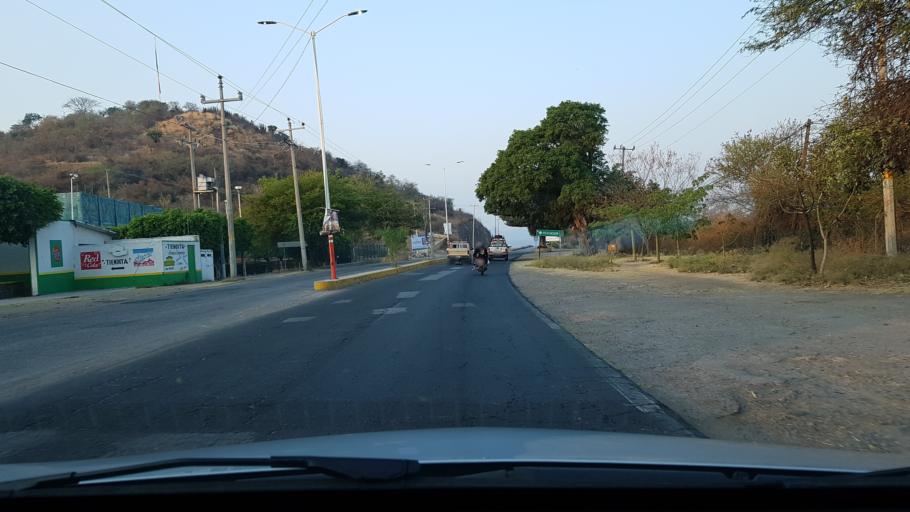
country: MX
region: Morelos
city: Jonacatepec de Leandro Valle
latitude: 18.6685
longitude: -98.8069
